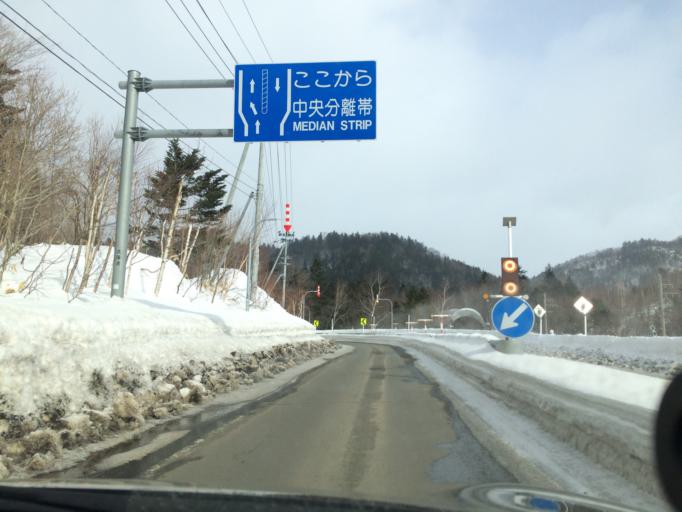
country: JP
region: Hokkaido
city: Shimo-furano
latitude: 43.0455
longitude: 142.4713
